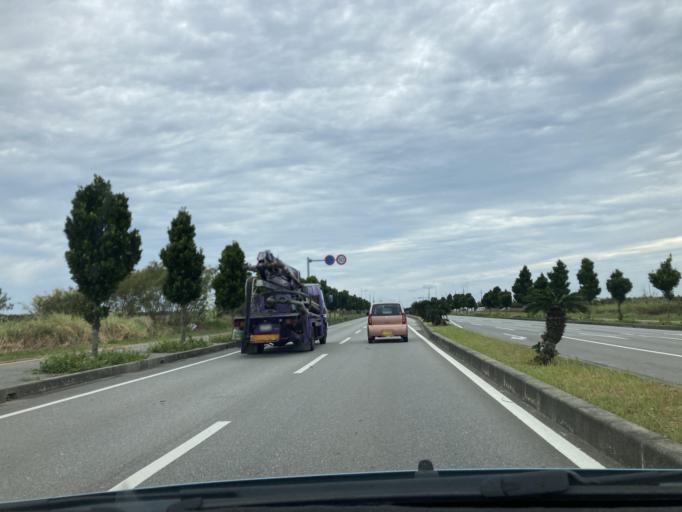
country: JP
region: Okinawa
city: Okinawa
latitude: 26.3934
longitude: 127.7433
